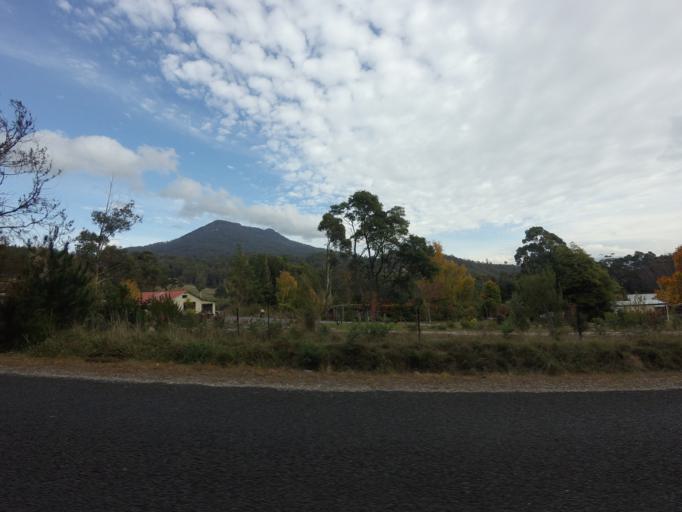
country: AU
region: Tasmania
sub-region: Meander Valley
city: Deloraine
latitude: -41.6200
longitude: 146.6984
